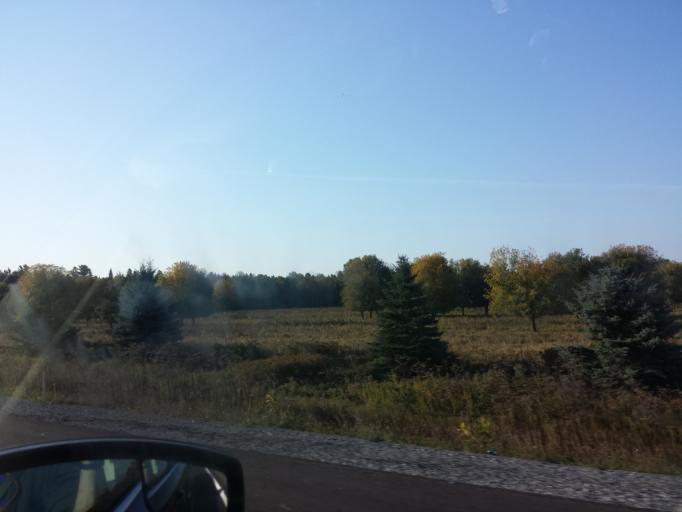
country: CA
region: Ontario
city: Bells Corners
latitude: 45.2470
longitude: -75.7783
